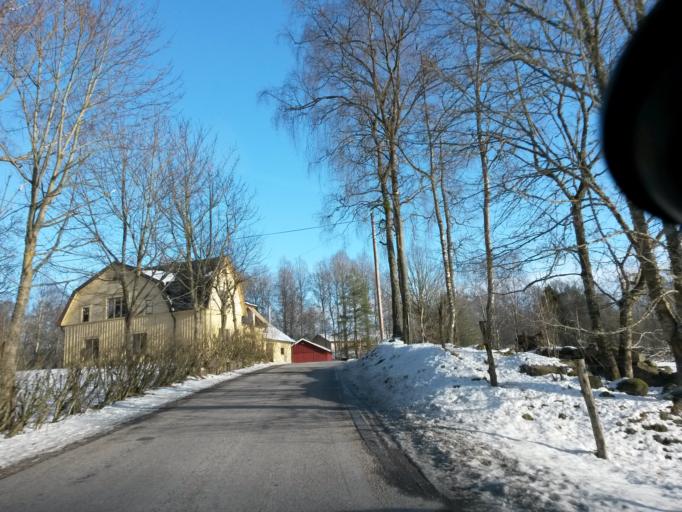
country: SE
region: Vaestra Goetaland
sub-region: Vargarda Kommun
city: Vargarda
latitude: 58.0325
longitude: 12.8813
